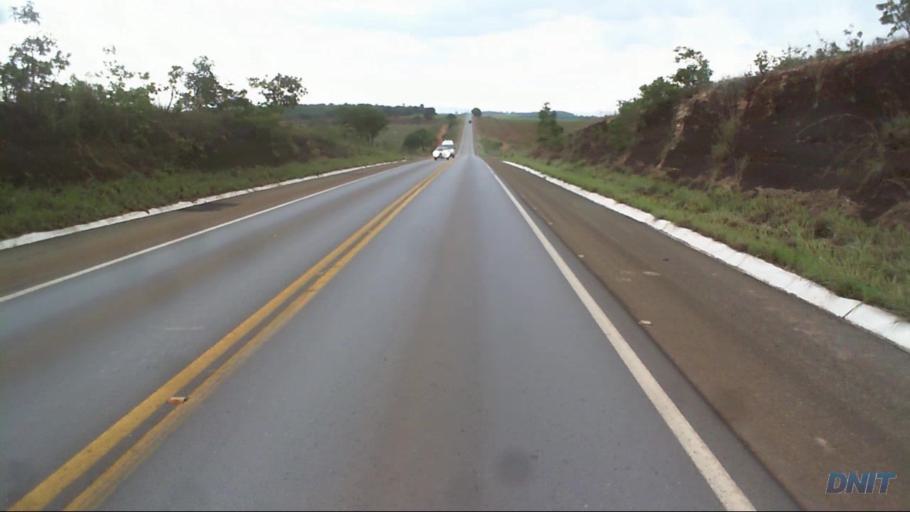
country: BR
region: Goias
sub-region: Uruacu
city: Uruacu
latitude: -14.6550
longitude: -49.1592
